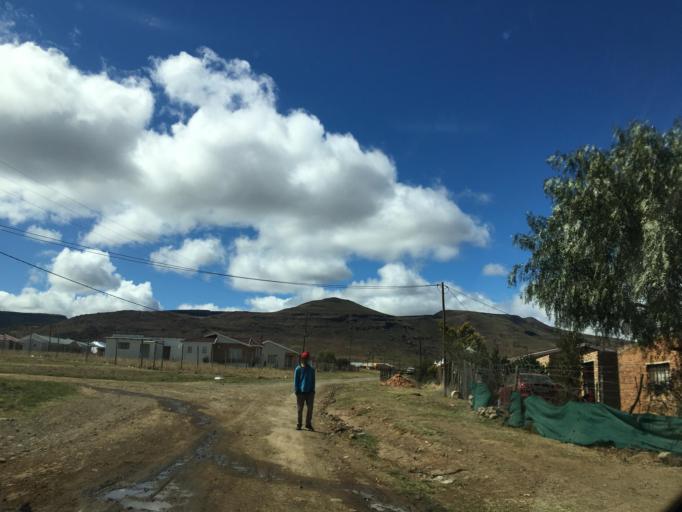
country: ZA
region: Eastern Cape
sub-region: Chris Hani District Municipality
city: Cala
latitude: -31.5380
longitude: 27.6904
